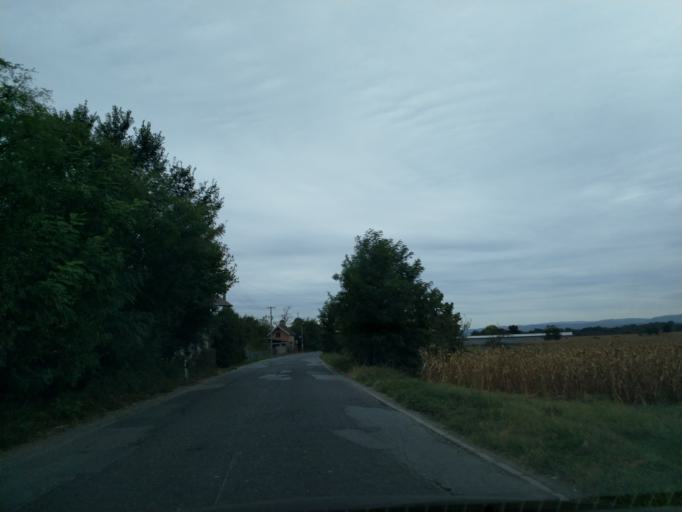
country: RS
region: Central Serbia
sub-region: Pomoravski Okrug
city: Paracin
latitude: 43.8318
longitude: 21.3646
